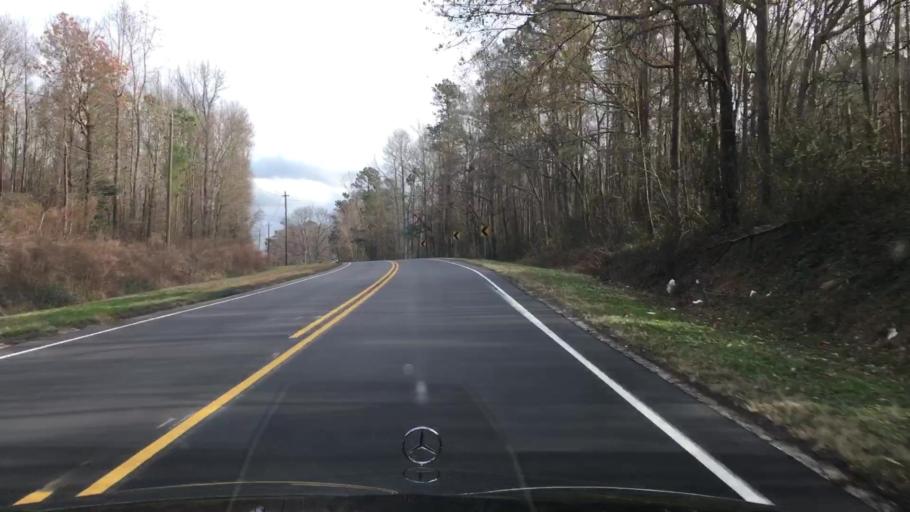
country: US
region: North Carolina
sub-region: Duplin County
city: Kenansville
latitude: 34.9615
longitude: -77.9930
